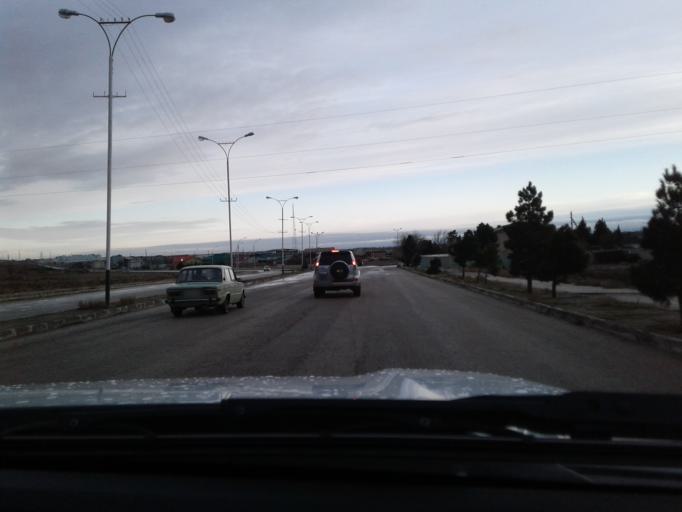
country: TM
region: Balkan
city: Balkanabat
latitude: 39.5328
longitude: 54.3533
